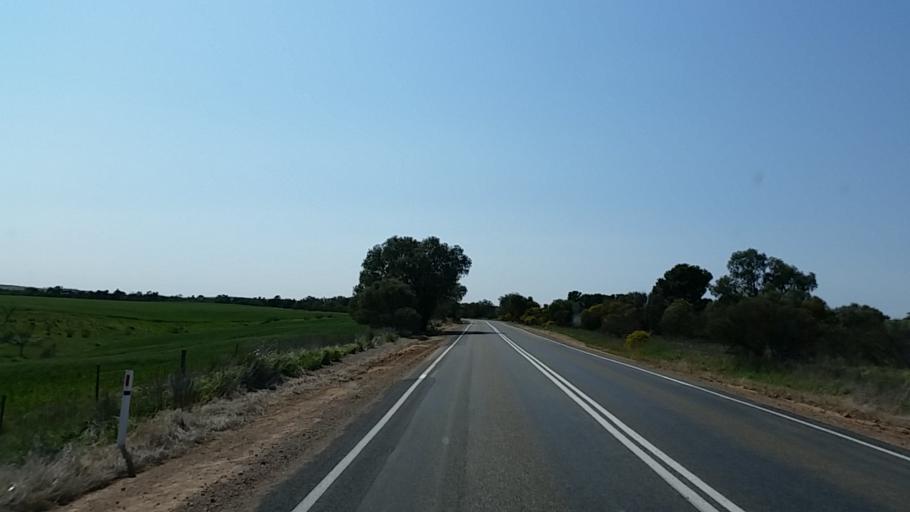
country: AU
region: South Australia
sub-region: Northern Areas
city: Jamestown
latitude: -33.2257
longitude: 138.4030
